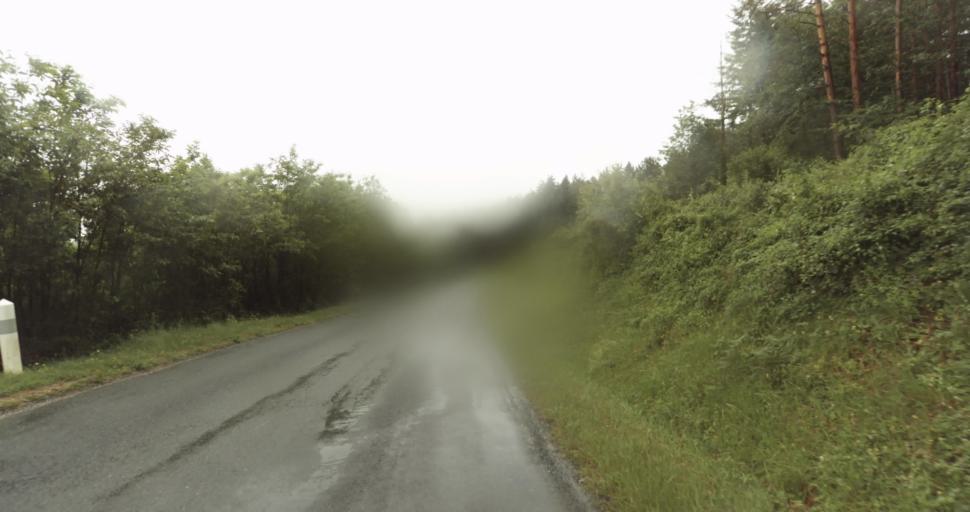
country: FR
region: Aquitaine
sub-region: Departement de la Dordogne
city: Beaumont-du-Perigord
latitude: 44.8100
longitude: 0.8566
